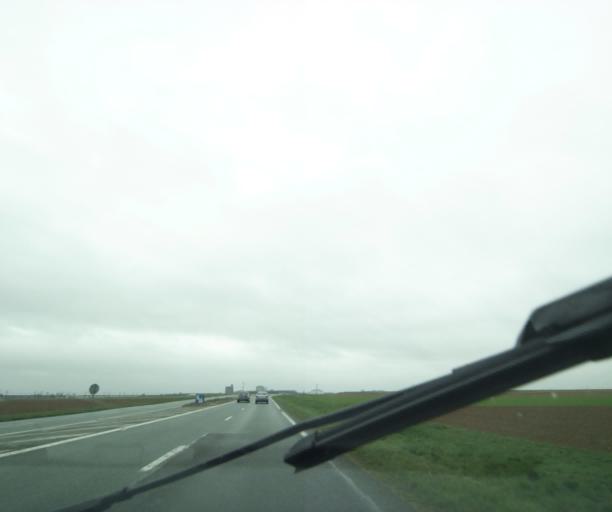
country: FR
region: Centre
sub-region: Departement du Loiret
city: Artenay
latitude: 48.1078
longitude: 1.8909
